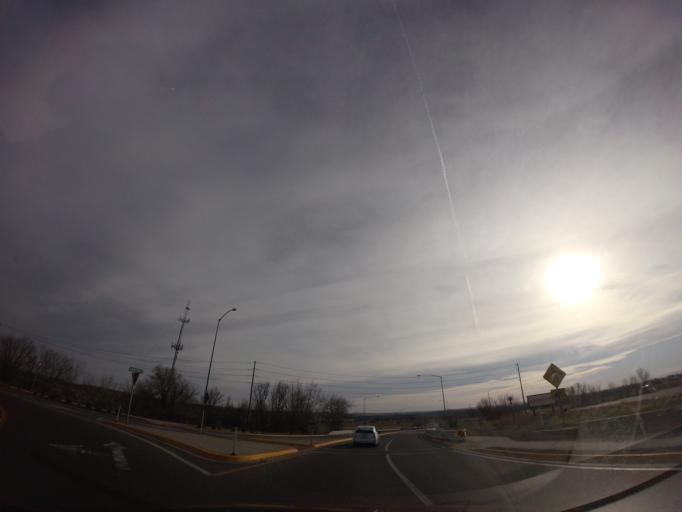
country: US
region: Montana
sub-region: Yellowstone County
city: Billings
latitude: 45.7400
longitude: -108.6177
